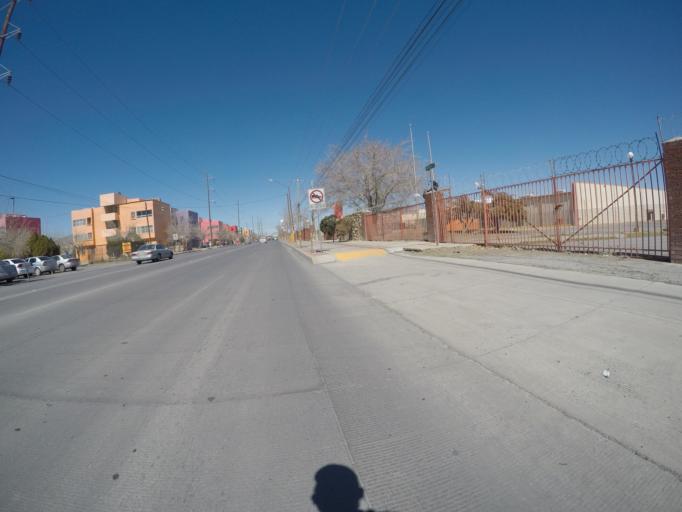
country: MX
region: Chihuahua
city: Ciudad Juarez
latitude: 31.7512
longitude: -106.4412
